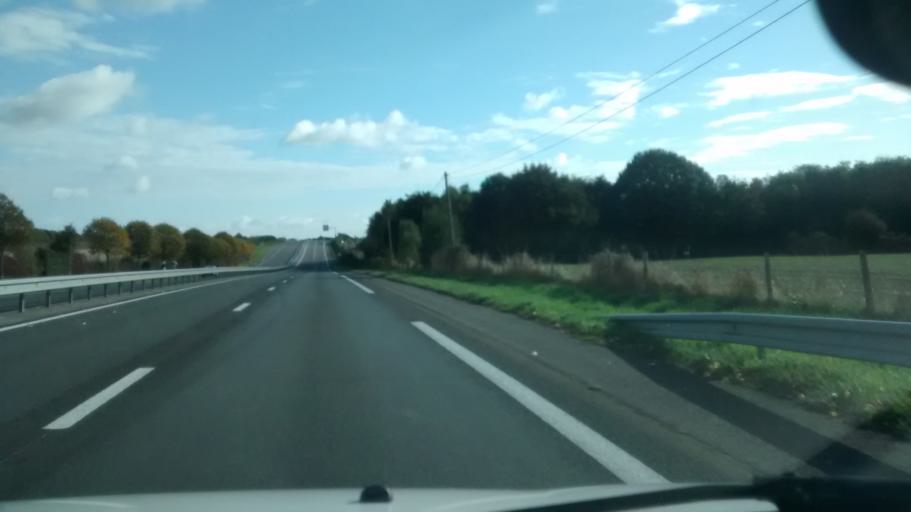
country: FR
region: Pays de la Loire
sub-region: Departement de Maine-et-Loire
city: Pouance
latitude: 47.7315
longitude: -1.1185
